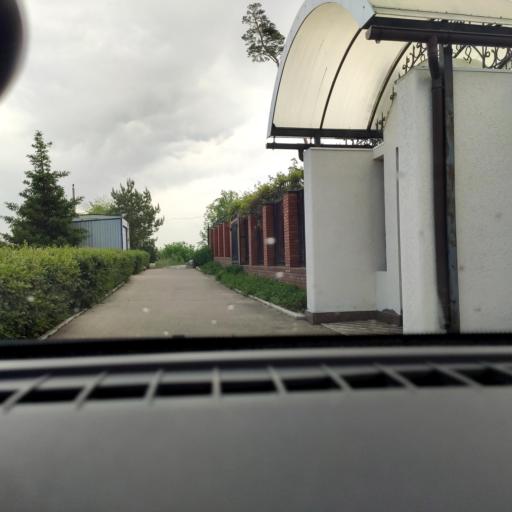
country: RU
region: Samara
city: Tol'yatti
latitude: 53.4797
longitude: 49.3664
